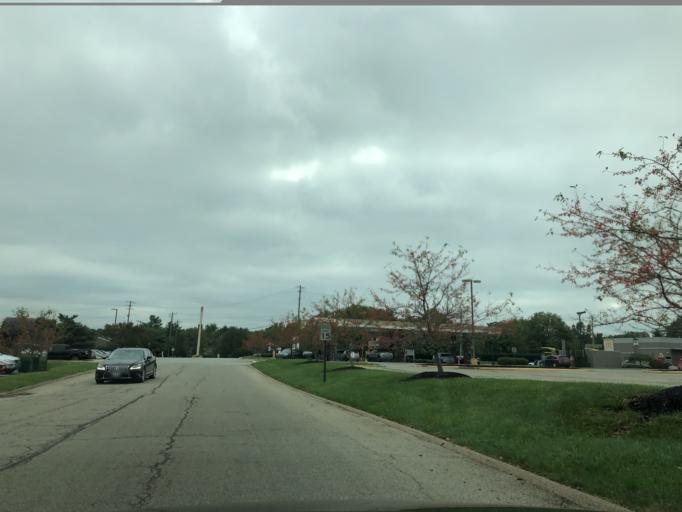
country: US
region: Ohio
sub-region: Warren County
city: Landen
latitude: 39.3100
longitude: -84.2764
